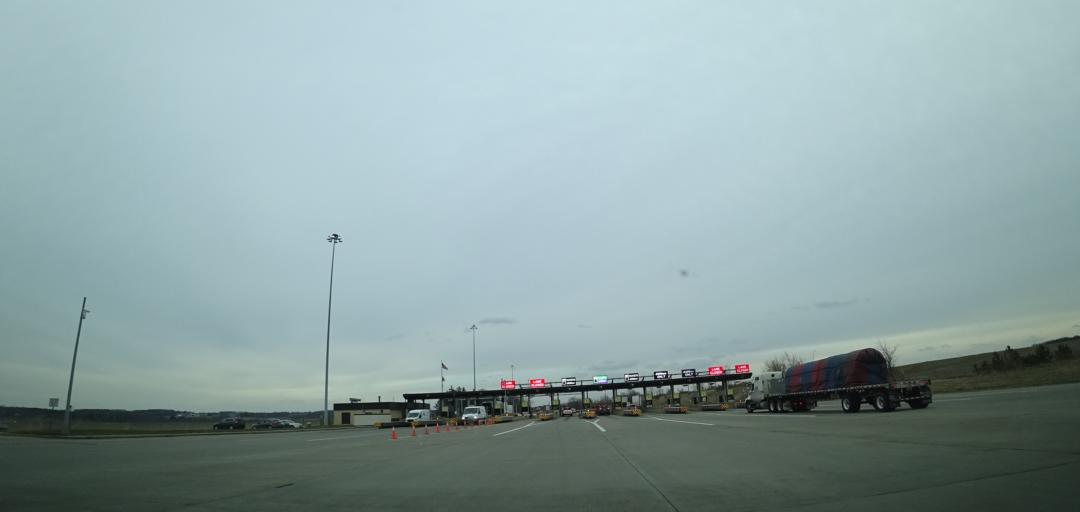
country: US
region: Ohio
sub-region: Mahoning County
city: New Middletown
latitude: 40.9247
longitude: -80.5580
